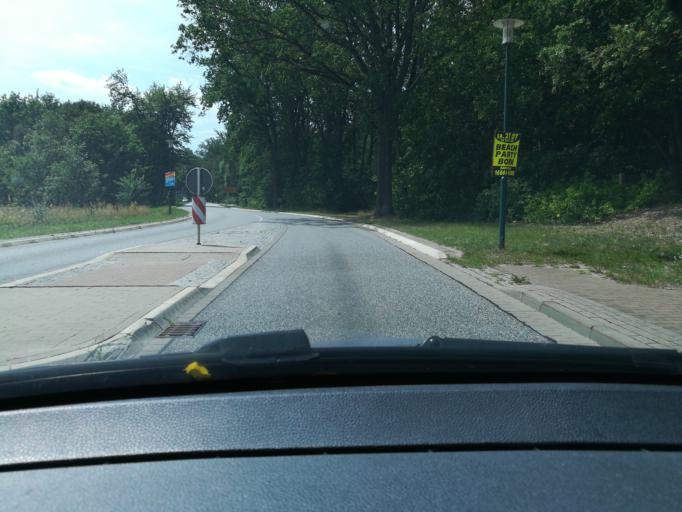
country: DE
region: Brandenburg
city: Wittstock
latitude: 53.0680
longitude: 12.4741
